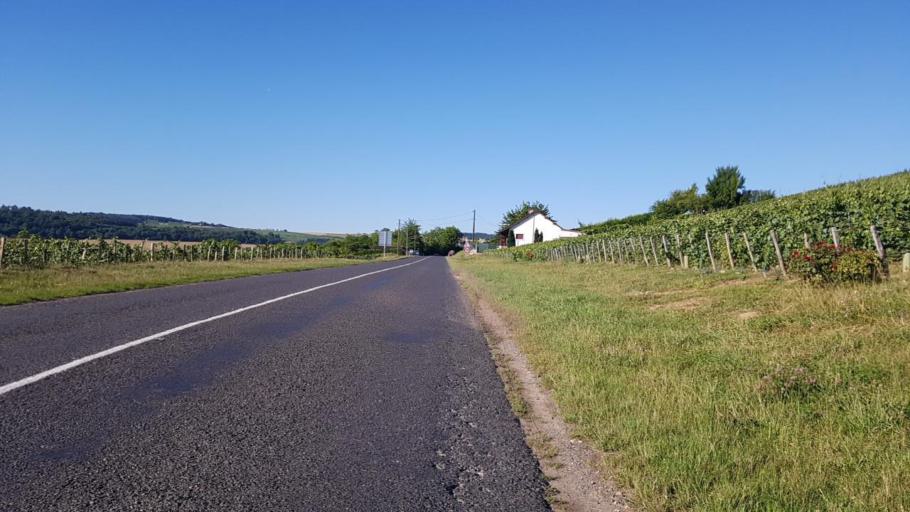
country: FR
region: Picardie
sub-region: Departement de l'Aisne
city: Chezy-sur-Marne
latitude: 49.0048
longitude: 3.3745
